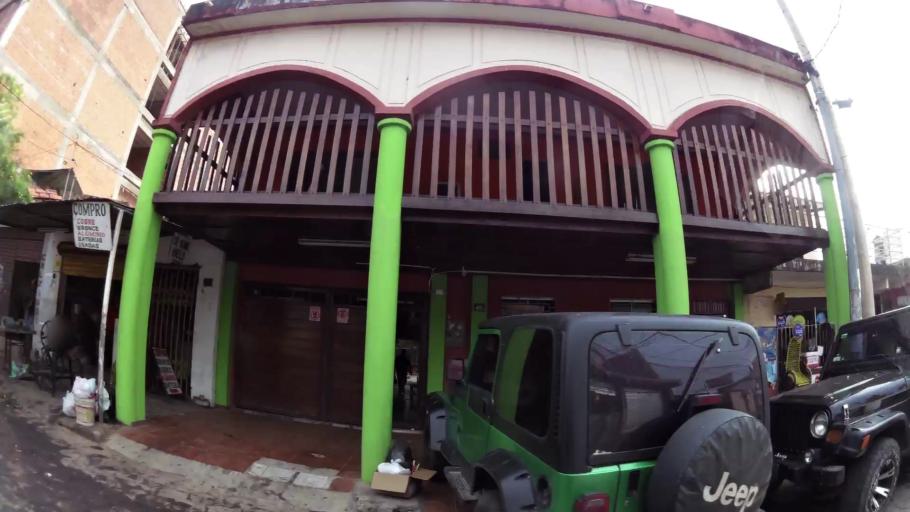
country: BO
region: Santa Cruz
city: Santa Cruz de la Sierra
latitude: -17.7776
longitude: -63.1744
